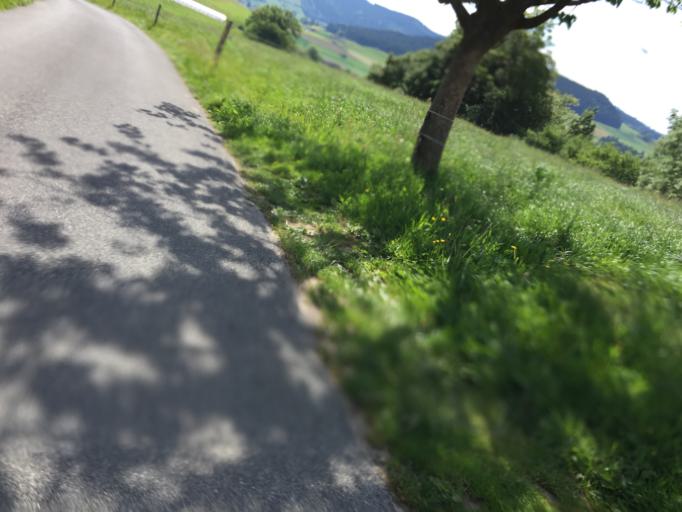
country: CH
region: Bern
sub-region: Bern-Mittelland District
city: Taegertschi
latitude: 46.8809
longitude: 7.5863
